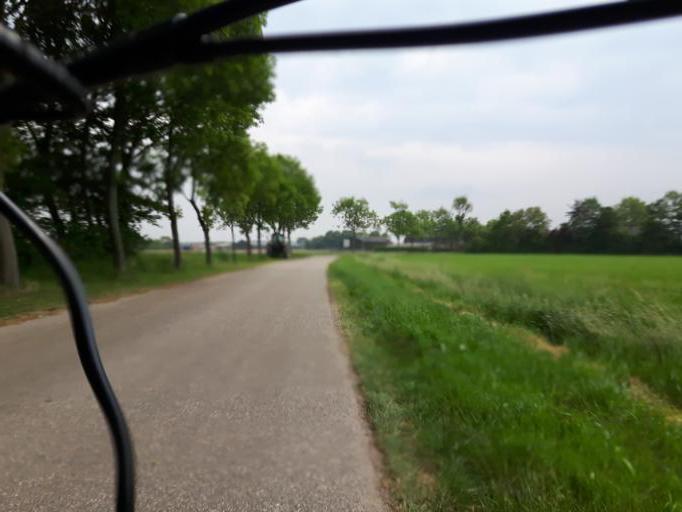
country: NL
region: North Brabant
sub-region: Gemeente Steenbergen
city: Kruisland
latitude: 51.5498
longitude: 4.4005
